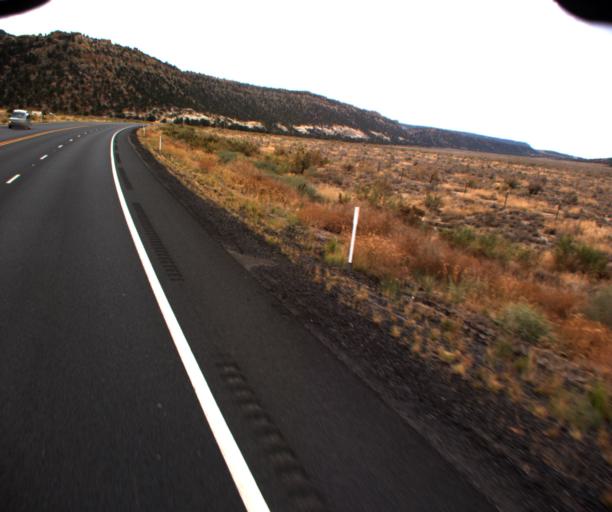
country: US
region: Arizona
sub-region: Navajo County
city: Kayenta
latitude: 36.5842
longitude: -110.4718
